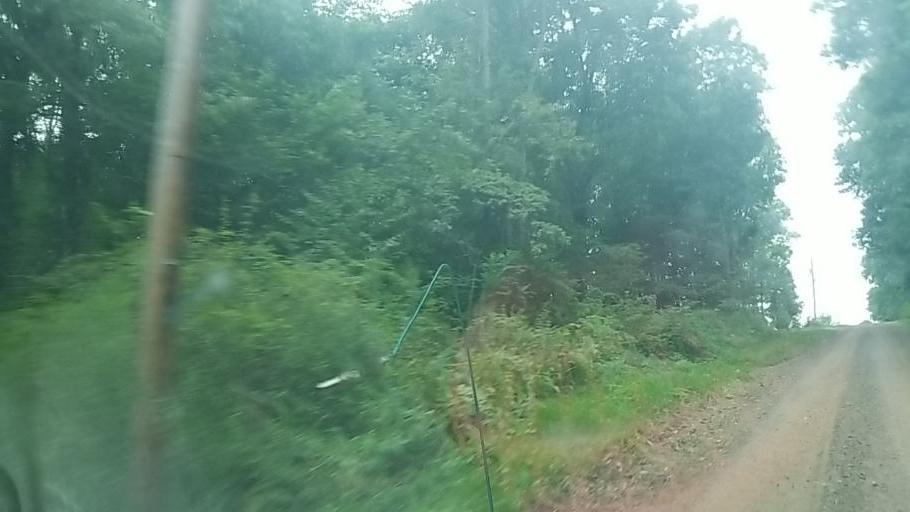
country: US
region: Ohio
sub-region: Knox County
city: Danville
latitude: 40.4985
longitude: -82.1519
